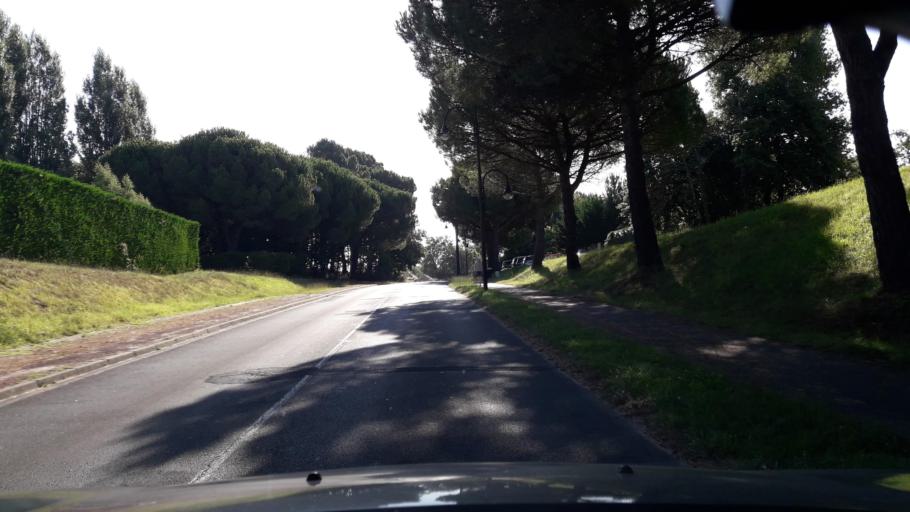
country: FR
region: Poitou-Charentes
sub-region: Departement de la Charente-Maritime
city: Les Mathes
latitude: 45.7148
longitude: -1.1459
